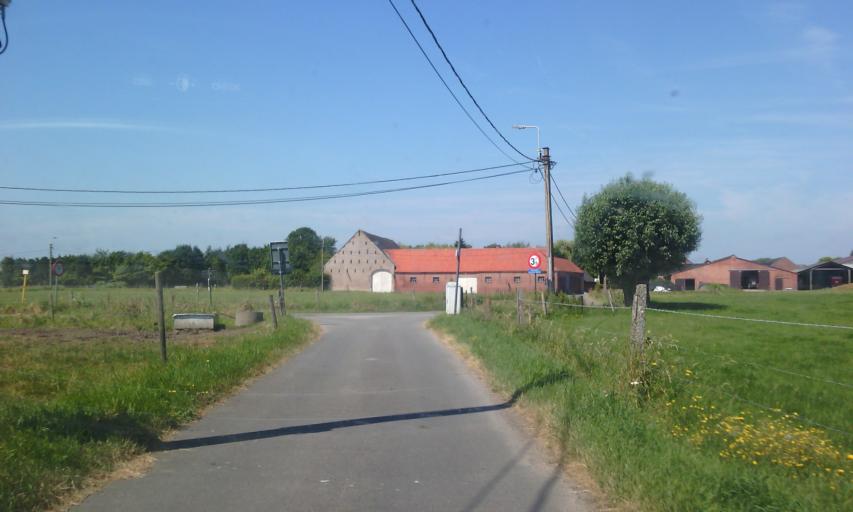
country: BE
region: Flanders
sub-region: Provincie Oost-Vlaanderen
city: Wichelen
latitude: 50.9974
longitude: 3.9963
